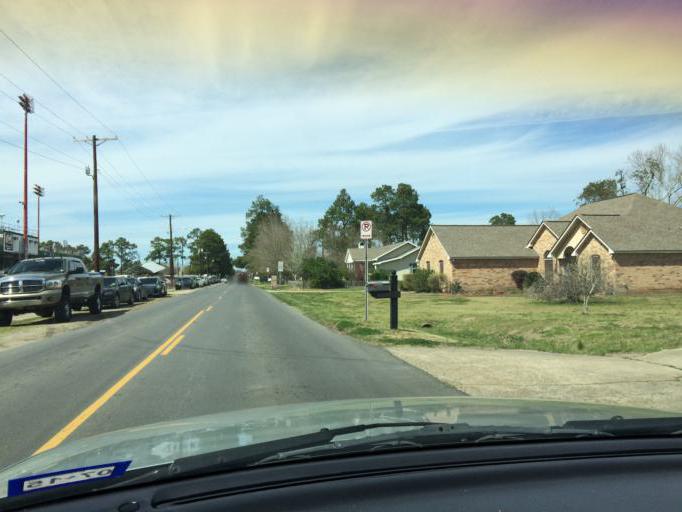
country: US
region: Louisiana
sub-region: Lafayette Parish
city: Lafayette
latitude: 30.2093
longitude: -92.0585
